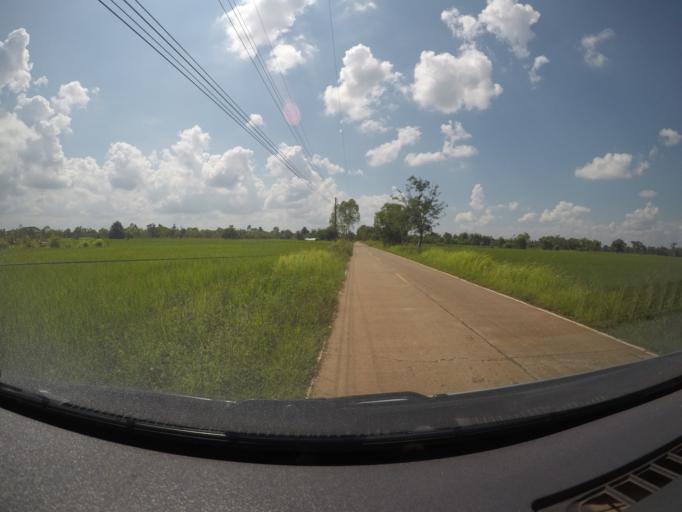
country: TH
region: Sakon Nakhon
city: Sakon Nakhon
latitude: 17.2117
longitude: 104.1203
